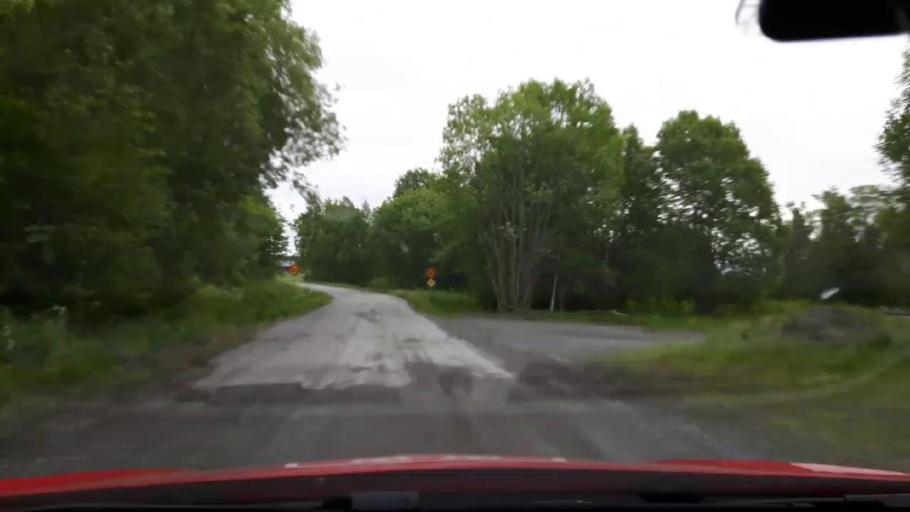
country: SE
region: Jaemtland
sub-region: Krokoms Kommun
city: Krokom
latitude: 63.2460
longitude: 14.5312
